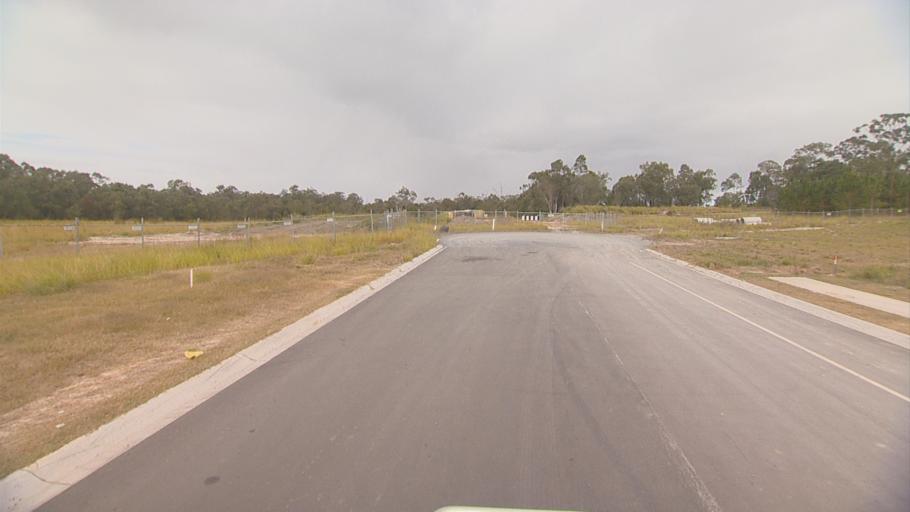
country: AU
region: Queensland
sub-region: Logan
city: Park Ridge South
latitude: -27.6921
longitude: 153.0482
